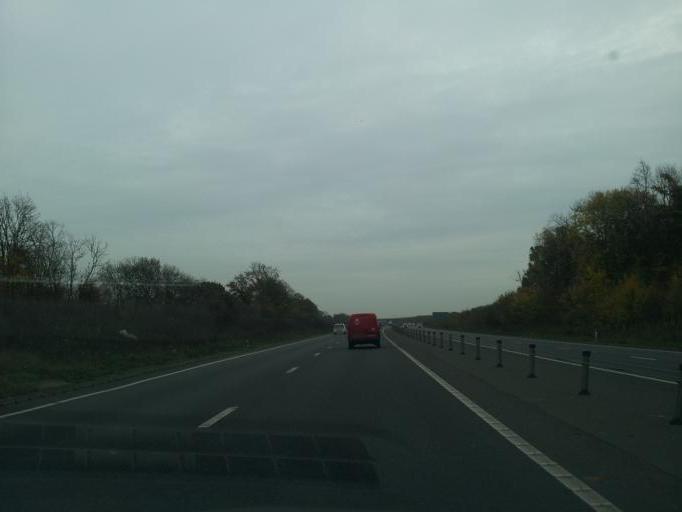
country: GB
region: England
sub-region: Cambridgeshire
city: Papworth Everard
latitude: 52.2231
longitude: -0.0570
